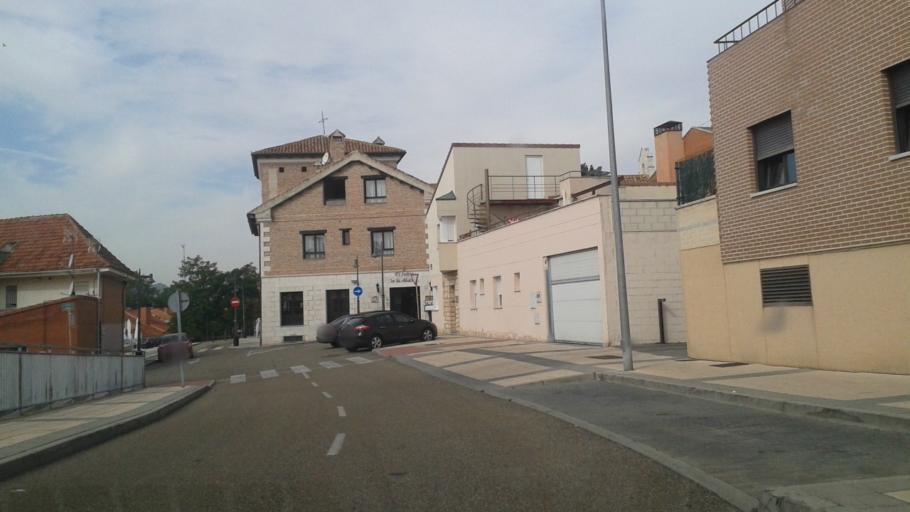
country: ES
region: Castille and Leon
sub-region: Provincia de Valladolid
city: Arroyo
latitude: 41.6100
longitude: -4.7960
